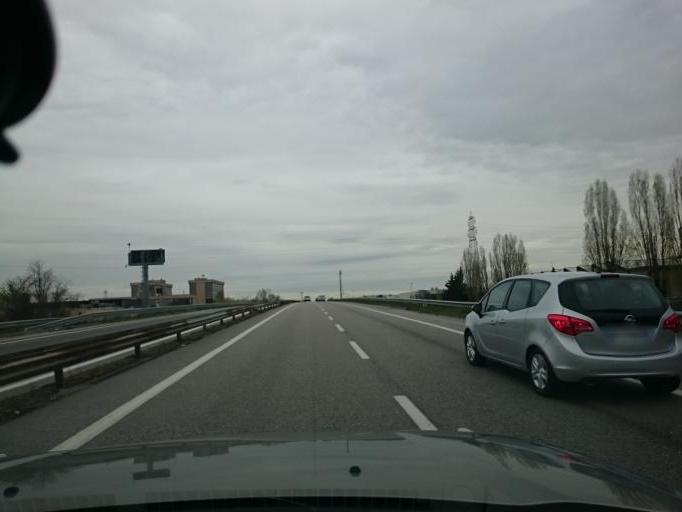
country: IT
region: Veneto
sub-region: Provincia di Padova
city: Ponte San Nicolo
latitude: 45.3940
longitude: 11.9275
